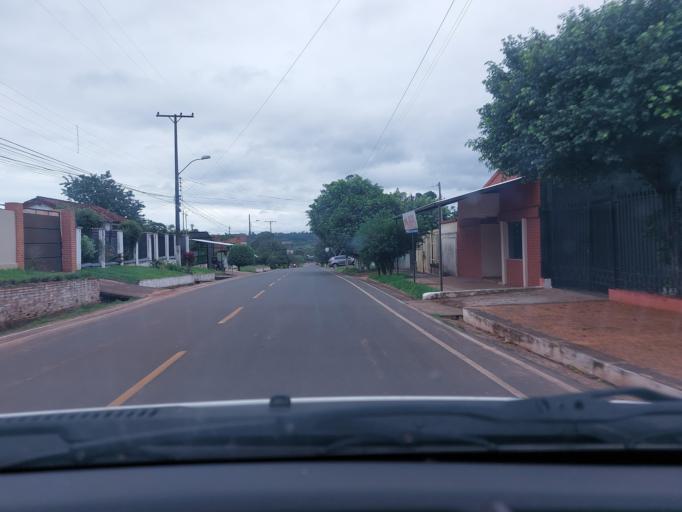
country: PY
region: San Pedro
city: Guayaybi
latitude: -24.6616
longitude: -56.4399
